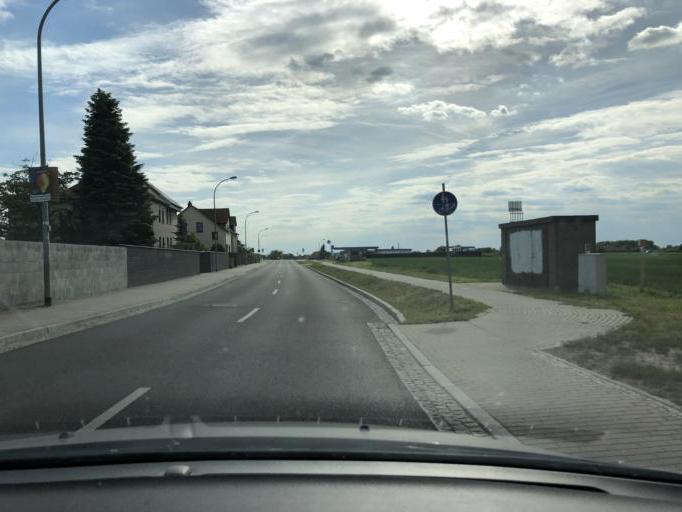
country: DE
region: Saxony
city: Brandis
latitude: 51.3306
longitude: 12.5964
